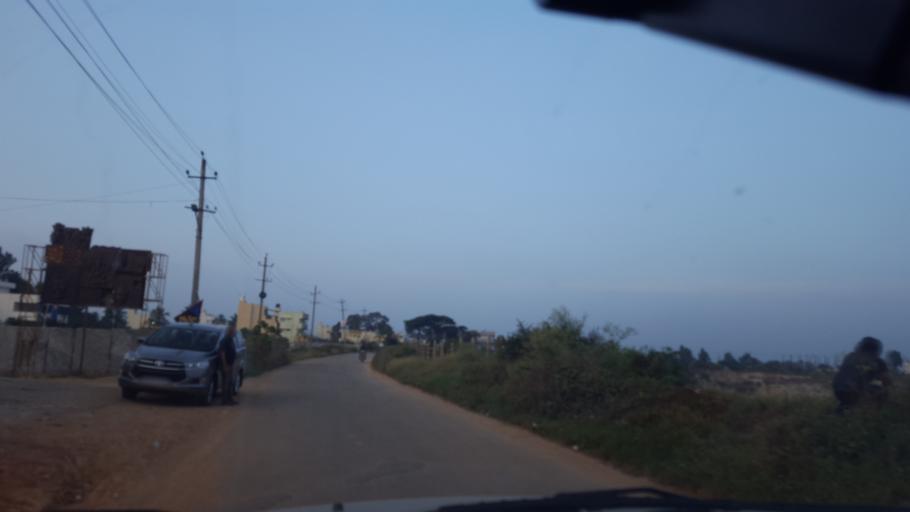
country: IN
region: Karnataka
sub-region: Bangalore Urban
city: Yelahanka
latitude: 13.0761
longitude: 77.6914
